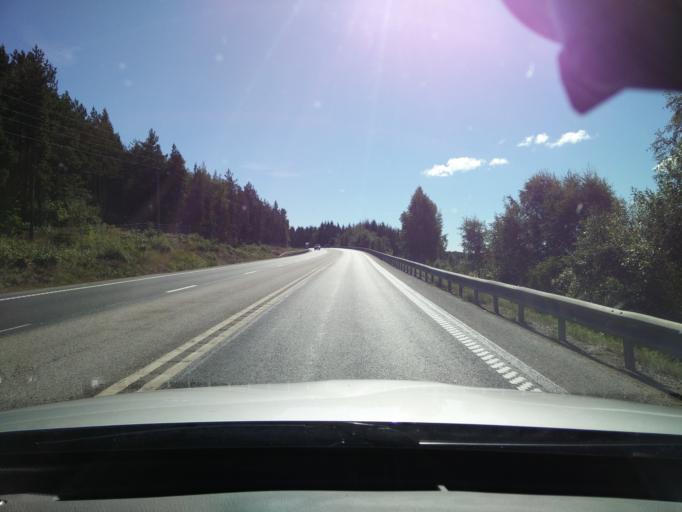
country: SE
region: Stockholm
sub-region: Lidingo
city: Lidingoe
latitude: 59.4548
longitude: 18.1752
